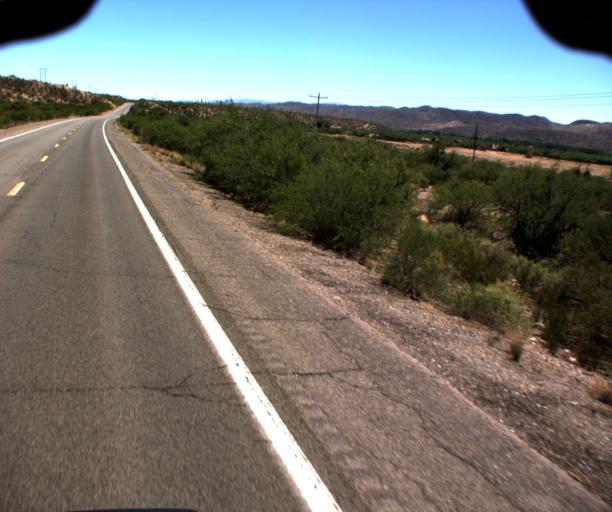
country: US
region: Arizona
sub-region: Pinal County
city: Mammoth
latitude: 32.8777
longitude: -110.7124
